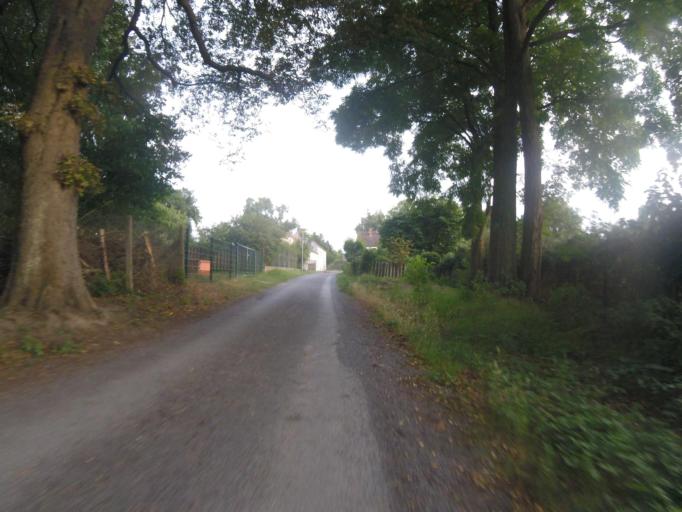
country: DE
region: Brandenburg
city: Zeuthen
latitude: 52.3420
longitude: 13.6139
